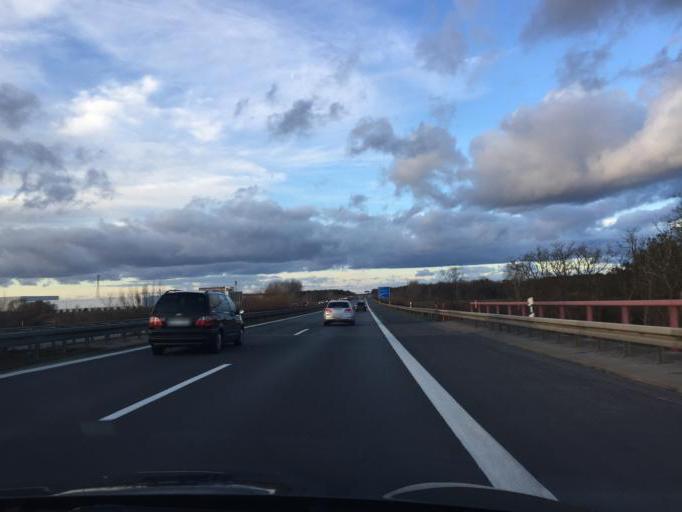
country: DE
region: Brandenburg
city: Mittenwalde
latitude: 52.2551
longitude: 13.5836
